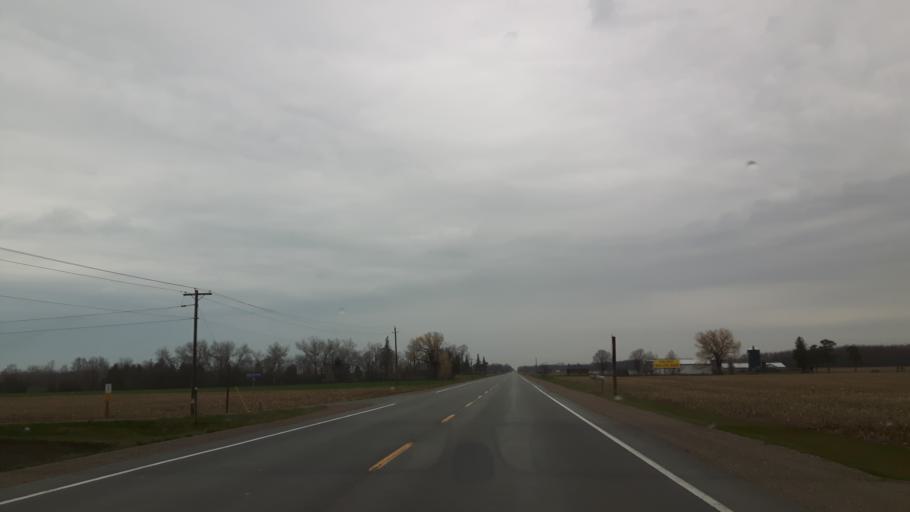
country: CA
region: Ontario
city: Goderich
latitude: 43.6290
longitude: -81.7056
